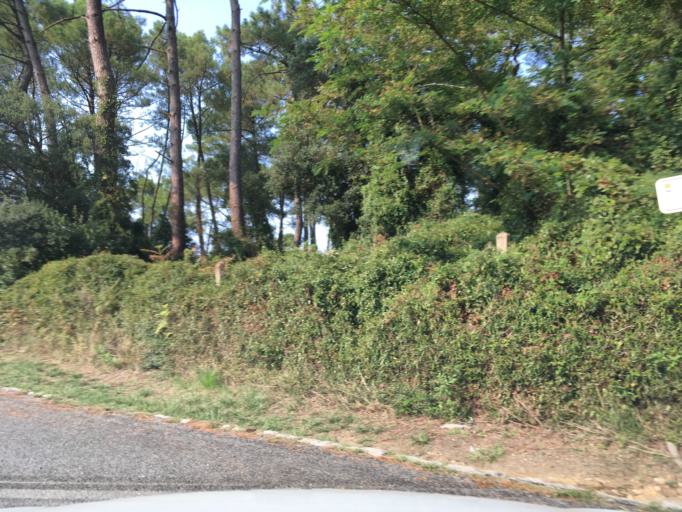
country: FR
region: Aquitaine
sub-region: Departement des Pyrenees-Atlantiques
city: Boucau
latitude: 43.5195
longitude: -1.4974
